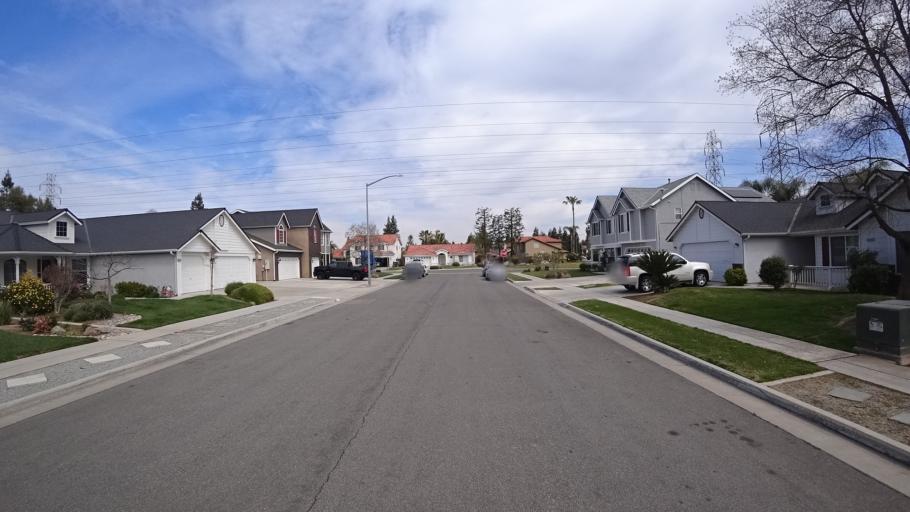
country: US
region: California
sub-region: Fresno County
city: Biola
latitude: 36.8327
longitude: -119.8956
